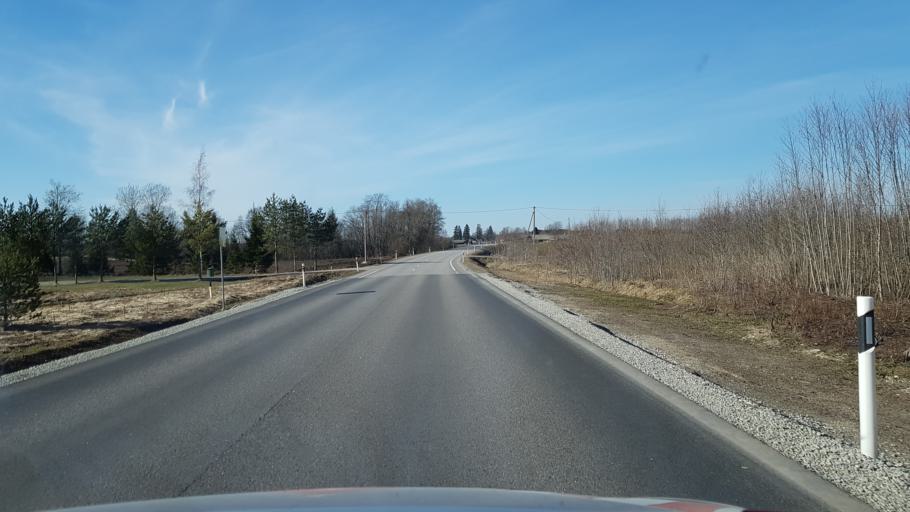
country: EE
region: Laeaene-Virumaa
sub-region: Vinni vald
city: Vinni
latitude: 59.1413
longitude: 26.5970
